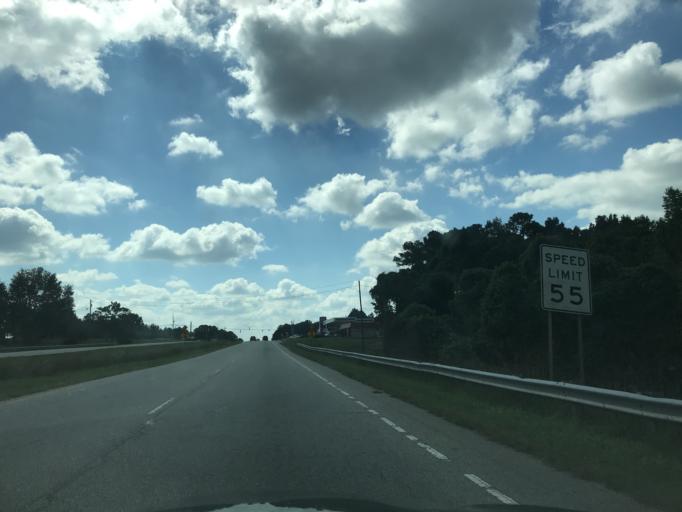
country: US
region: North Carolina
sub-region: Franklin County
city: Franklinton
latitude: 36.1000
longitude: -78.4675
